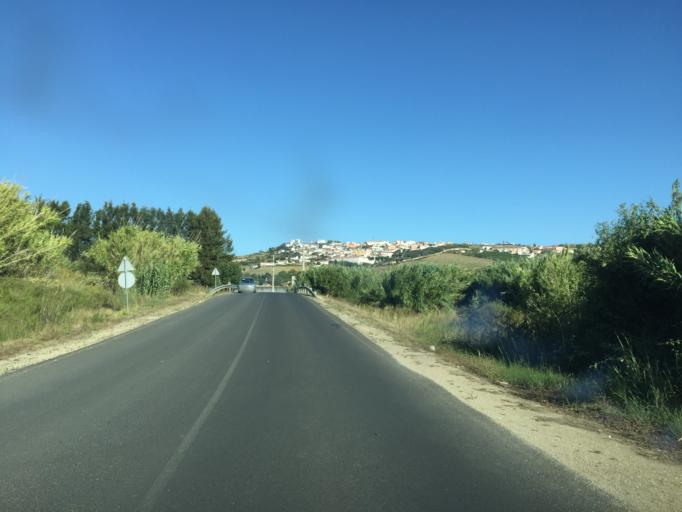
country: PT
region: Lisbon
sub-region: Torres Vedras
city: Torres Vedras
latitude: 39.0951
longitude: -9.2893
